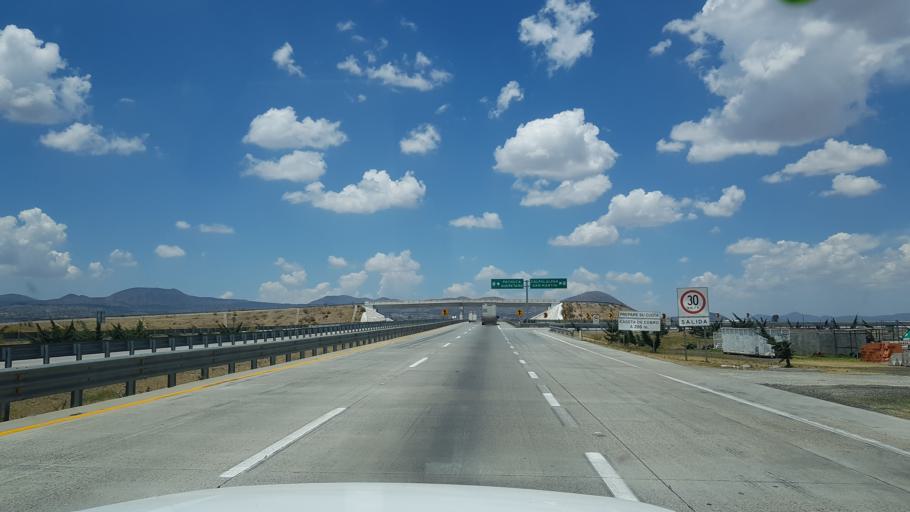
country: MX
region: Hidalgo
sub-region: Emiliano Zapata
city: Emiliano Zapata
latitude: 19.6202
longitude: -98.5484
